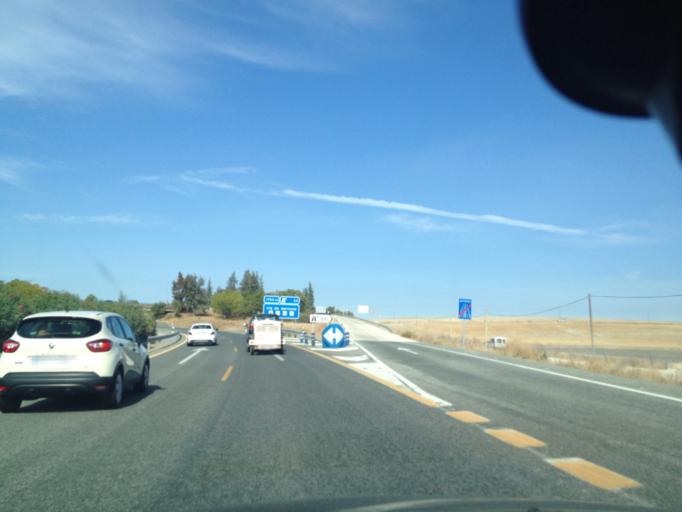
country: ES
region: Andalusia
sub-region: Provincia de Sevilla
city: La Puebla de Cazalla
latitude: 37.2303
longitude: -5.2999
